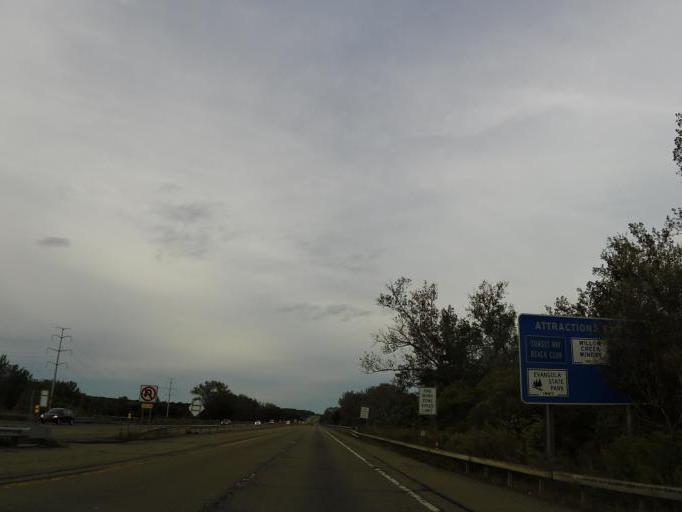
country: US
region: New York
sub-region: Erie County
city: Lake Erie Beach
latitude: 42.5643
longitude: -79.0928
